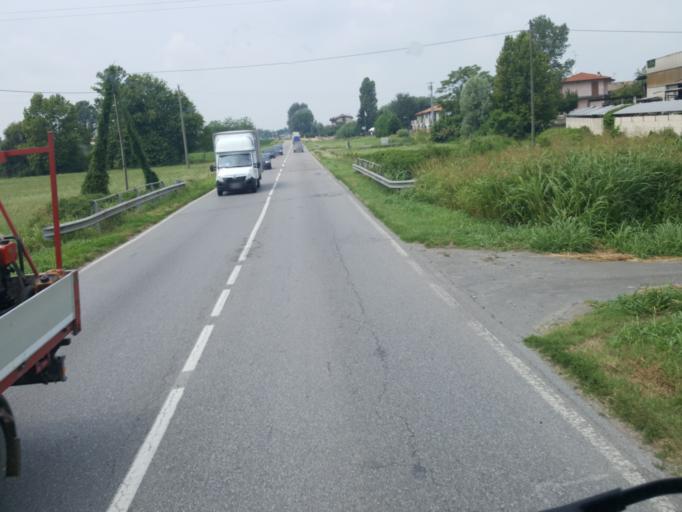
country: IT
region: Lombardy
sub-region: Provincia di Bergamo
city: Arzago d'Adda
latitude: 45.4772
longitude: 9.5696
